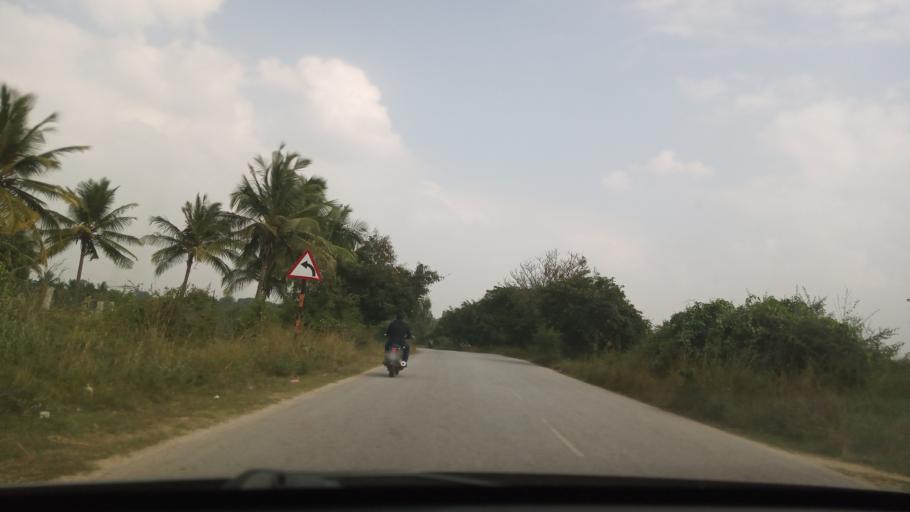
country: IN
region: Andhra Pradesh
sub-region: Chittoor
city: Madanapalle
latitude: 13.6447
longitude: 78.7220
